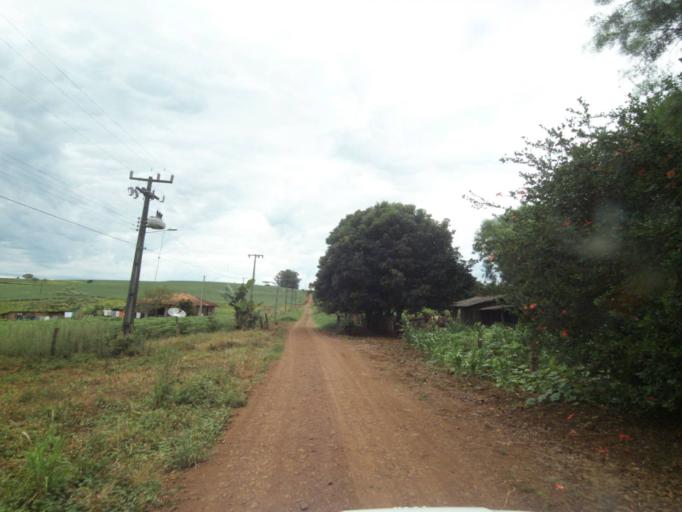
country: BR
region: Parana
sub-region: Guaraniacu
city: Guaraniacu
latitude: -24.9243
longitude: -52.9371
